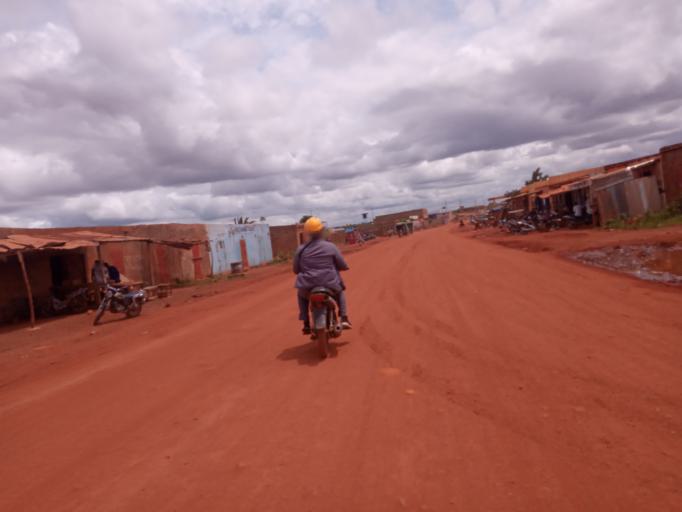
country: ML
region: Bamako
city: Bamako
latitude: 12.5375
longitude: -7.9943
